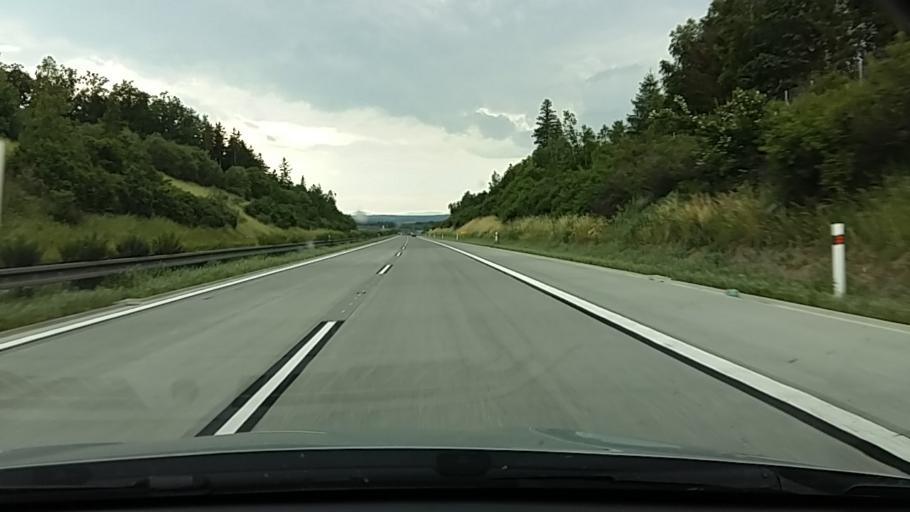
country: CZ
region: Plzensky
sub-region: Okres Tachov
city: Kladruby
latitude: 49.7057
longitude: 13.0071
